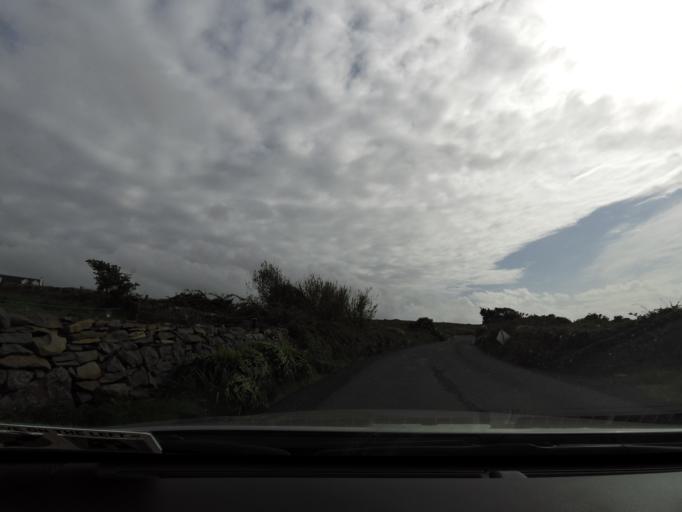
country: IE
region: Connaught
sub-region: County Galway
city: Bearna
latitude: 53.0488
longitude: -9.3424
